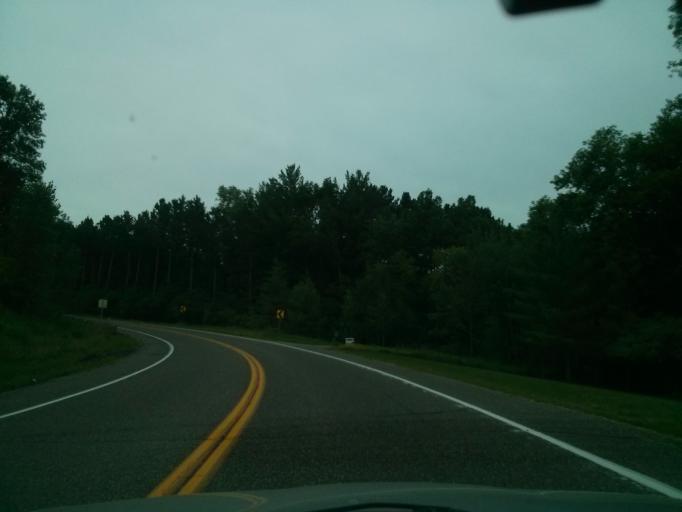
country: US
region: Minnesota
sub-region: Washington County
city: Afton
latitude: 44.8623
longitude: -92.8018
